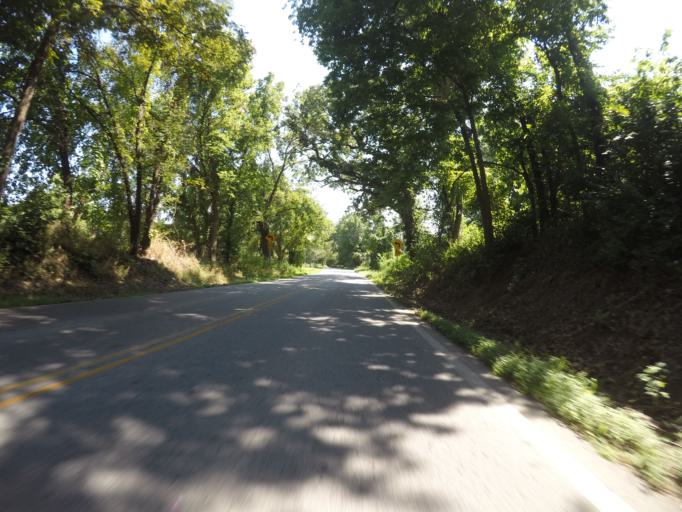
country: US
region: Kansas
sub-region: Leavenworth County
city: Lansing
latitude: 39.2655
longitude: -94.8895
